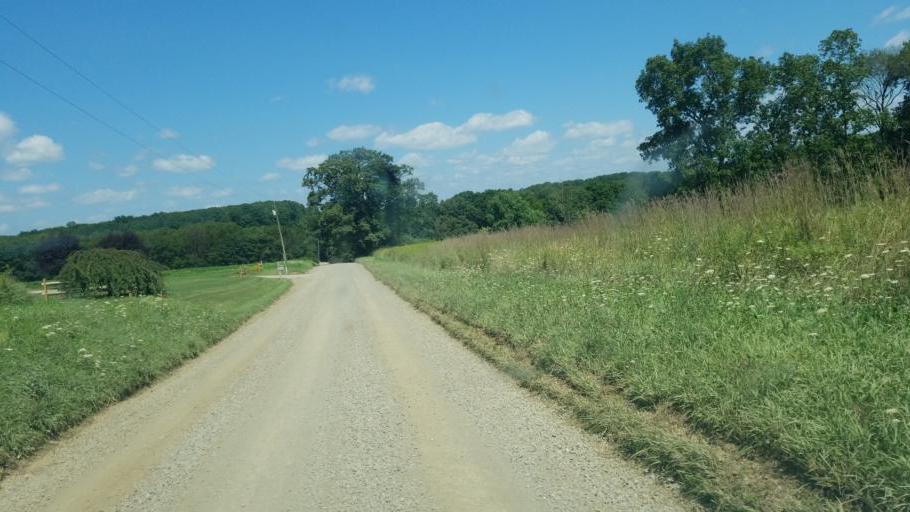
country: US
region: Pennsylvania
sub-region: Clarion County
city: Knox
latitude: 41.2054
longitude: -79.5276
